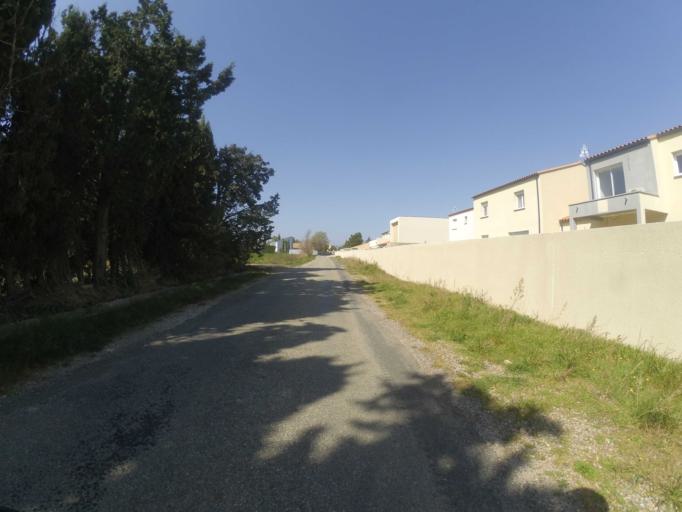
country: FR
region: Languedoc-Roussillon
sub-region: Departement des Pyrenees-Orientales
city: Corneilla-la-Riviere
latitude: 42.6774
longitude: 2.7478
